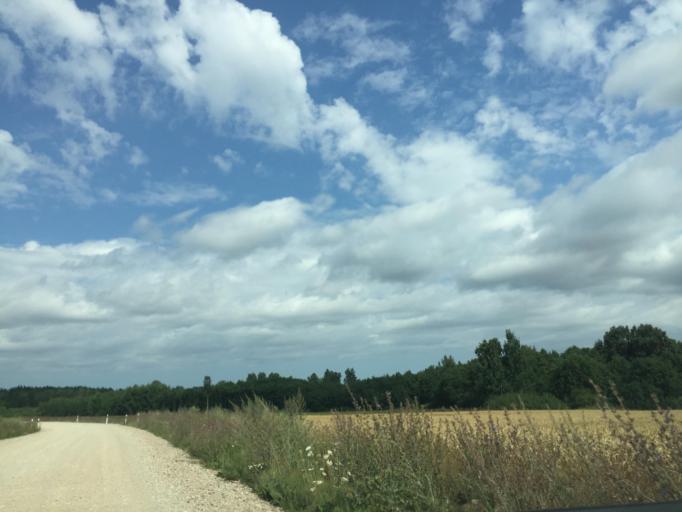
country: LV
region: Kandava
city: Kandava
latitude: 57.0020
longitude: 22.8562
